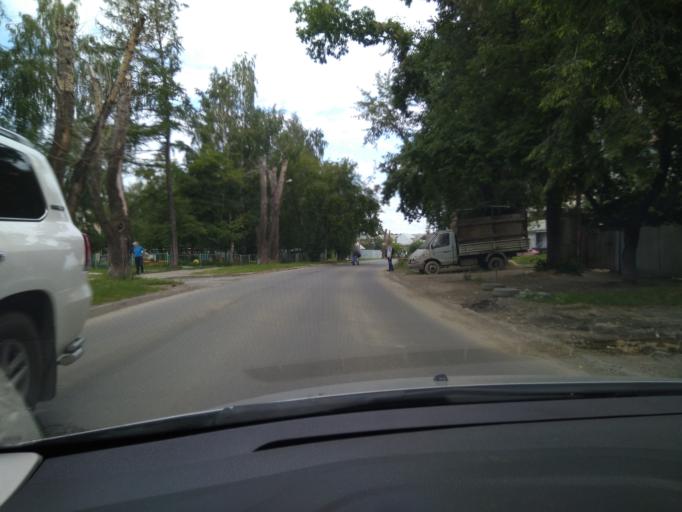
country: RU
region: Sverdlovsk
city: Yekaterinburg
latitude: 56.9096
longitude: 60.6013
